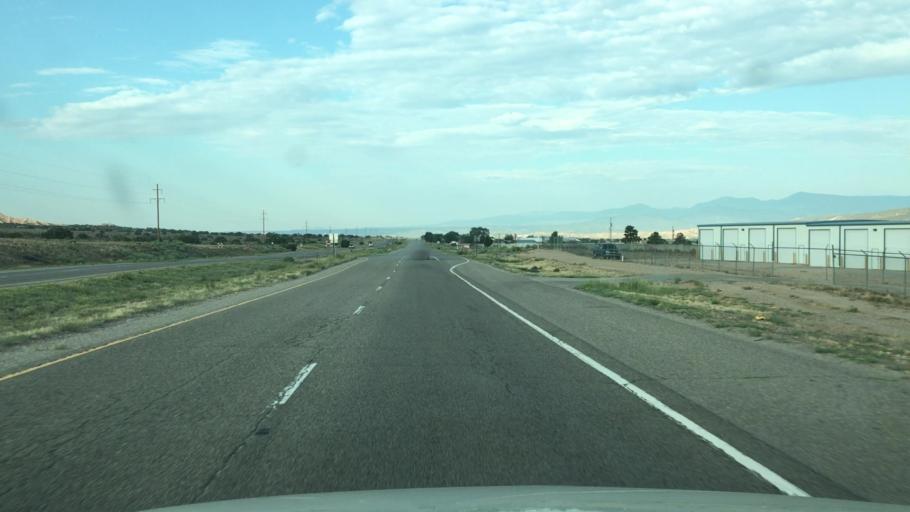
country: US
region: New Mexico
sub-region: Rio Arriba County
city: Ohkay Owingeh
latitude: 36.1348
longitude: -105.9972
